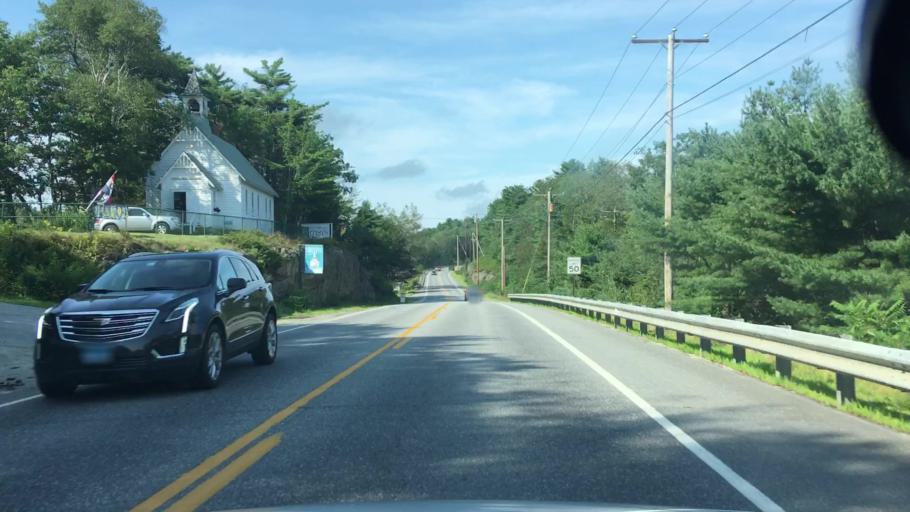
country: US
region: Maine
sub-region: Cumberland County
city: Harpswell Center
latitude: 43.8048
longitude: -69.9324
